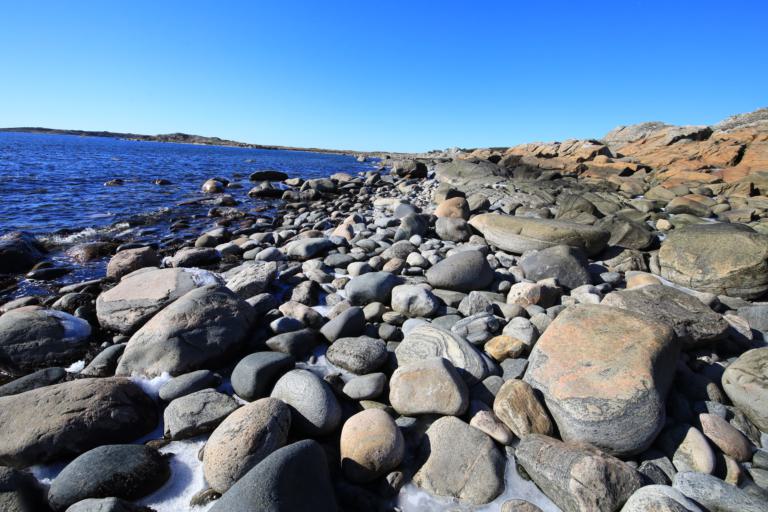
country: SE
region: Halland
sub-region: Kungsbacka Kommun
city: Frillesas
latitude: 57.2273
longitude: 12.1180
